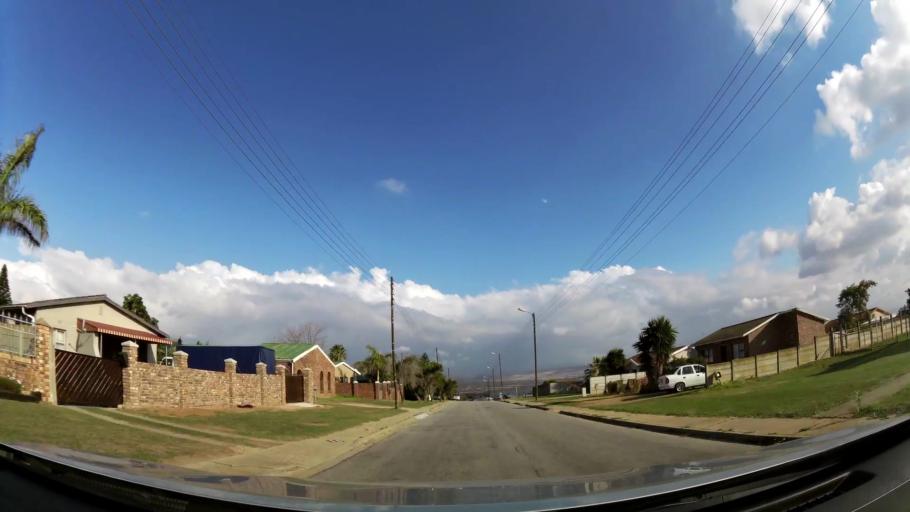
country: ZA
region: Eastern Cape
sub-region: Nelson Mandela Bay Metropolitan Municipality
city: Uitenhage
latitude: -33.7739
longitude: 25.4279
